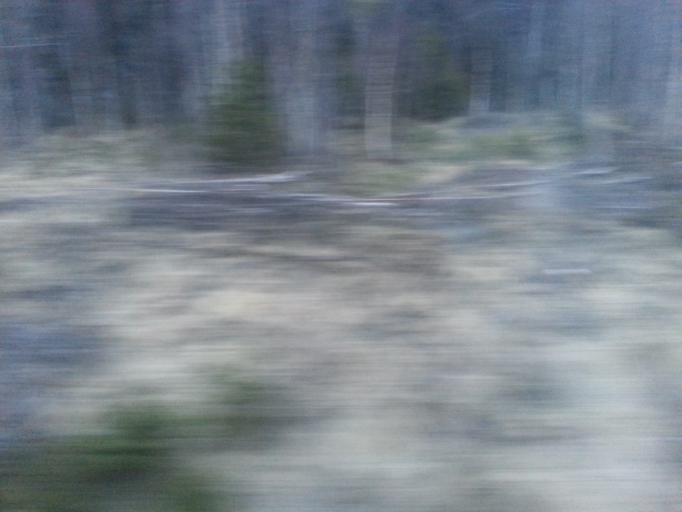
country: NO
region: Sor-Trondelag
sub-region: Rennebu
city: Berkak
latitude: 62.7693
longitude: 9.9899
